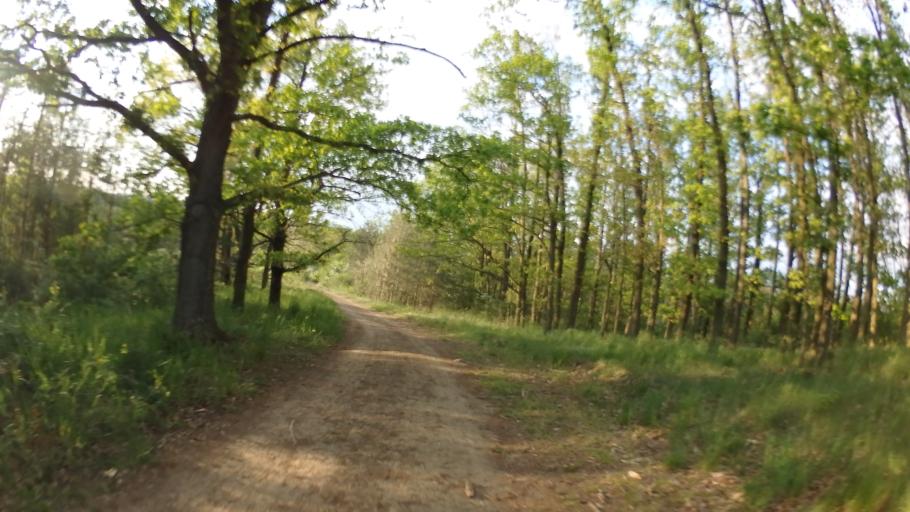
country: CZ
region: South Moravian
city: Moravany
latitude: 49.1365
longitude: 16.5647
